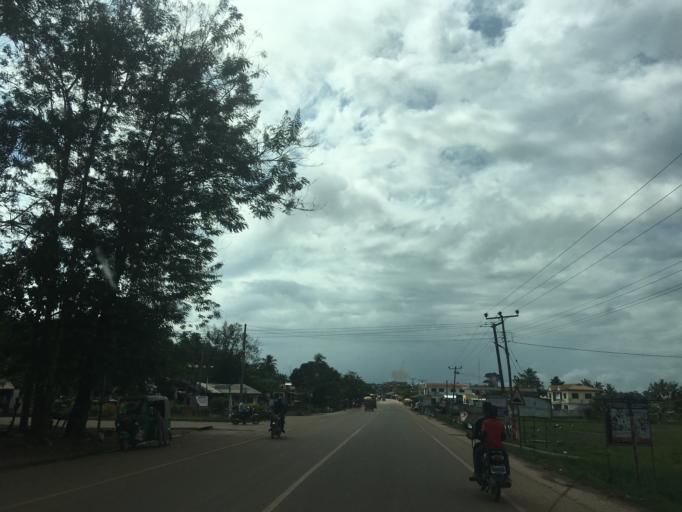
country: GH
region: Western
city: Wassa-Akropong
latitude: 5.8038
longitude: -2.4315
